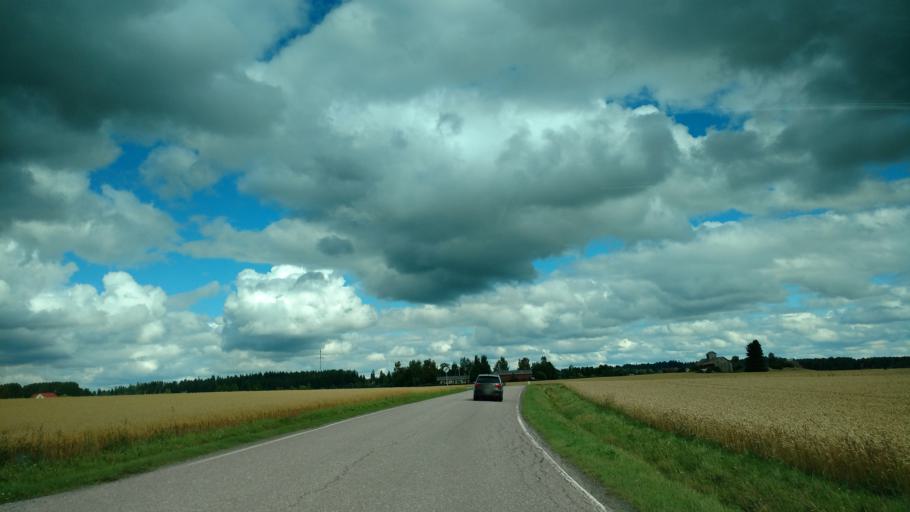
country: FI
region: Haeme
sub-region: Forssa
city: Ypaejae
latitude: 60.7883
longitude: 23.2712
